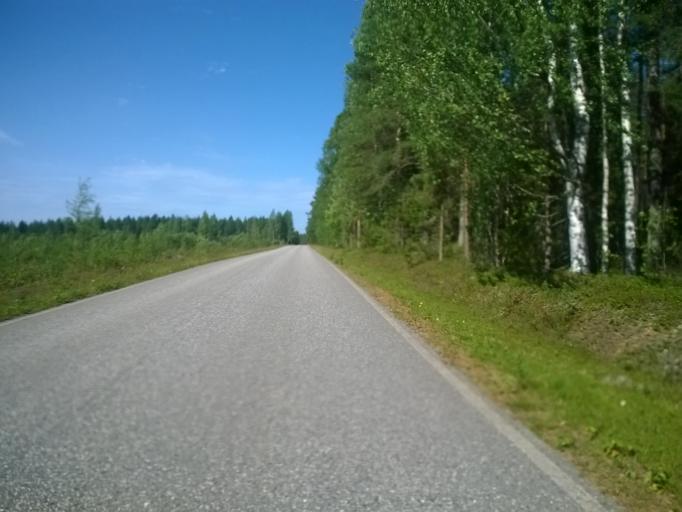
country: FI
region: Kainuu
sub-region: Kehys-Kainuu
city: Kuhmo
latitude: 64.1341
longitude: 29.4338
